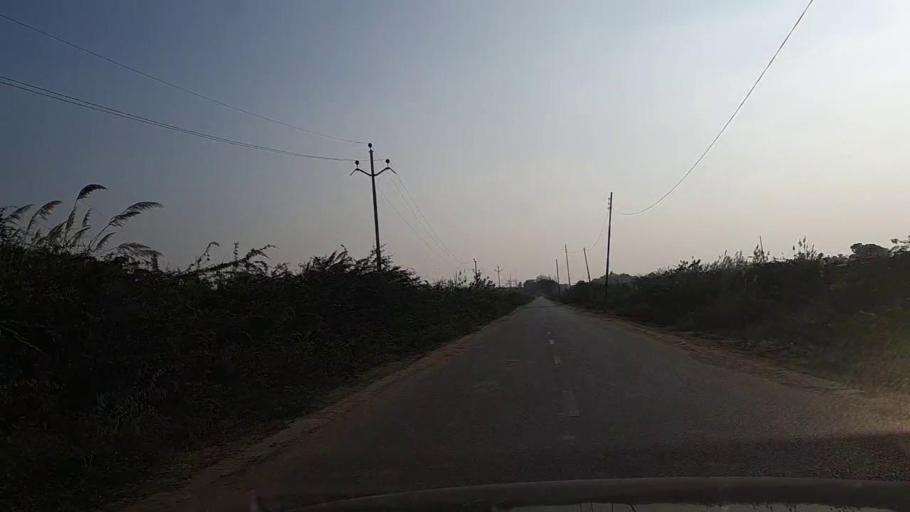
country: PK
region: Sindh
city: Gharo
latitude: 24.7833
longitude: 67.5124
